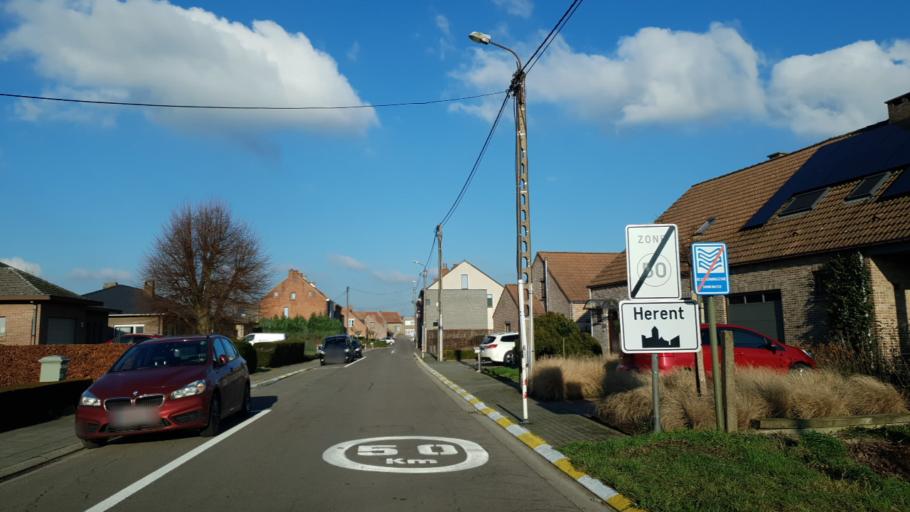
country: BE
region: Flanders
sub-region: Provincie Vlaams-Brabant
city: Herent
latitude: 50.9204
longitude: 4.6912
